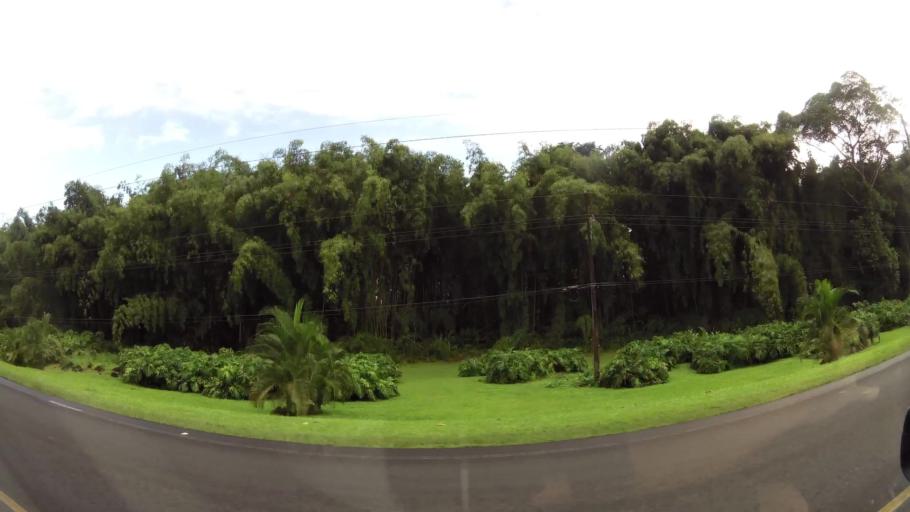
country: CR
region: Limon
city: Pocora
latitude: 10.1751
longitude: -83.6145
